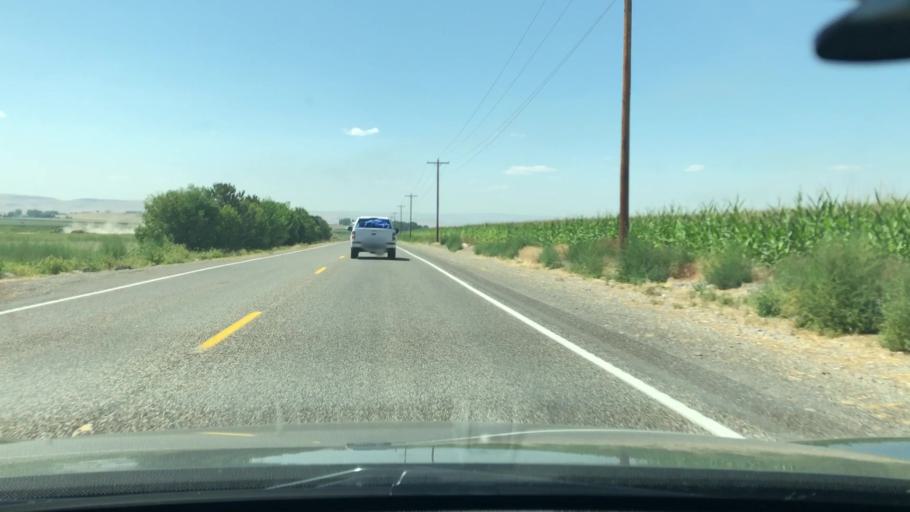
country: US
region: Idaho
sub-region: Owyhee County
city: Marsing
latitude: 43.5453
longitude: -116.8724
